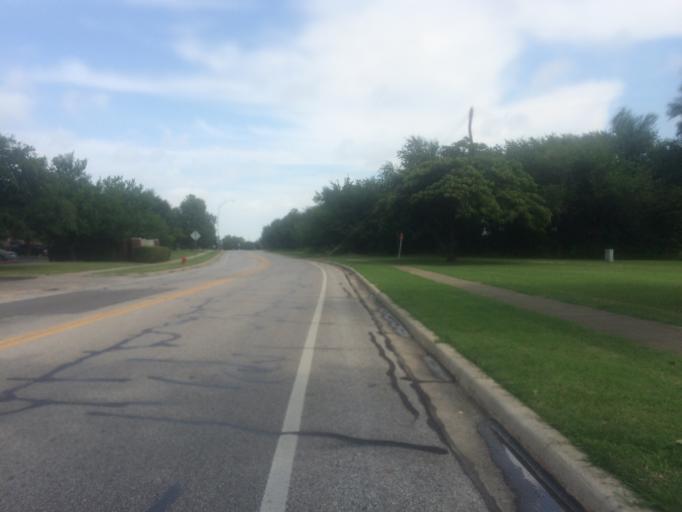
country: US
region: Oklahoma
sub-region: Cleveland County
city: Norman
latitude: 35.1889
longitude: -97.4241
